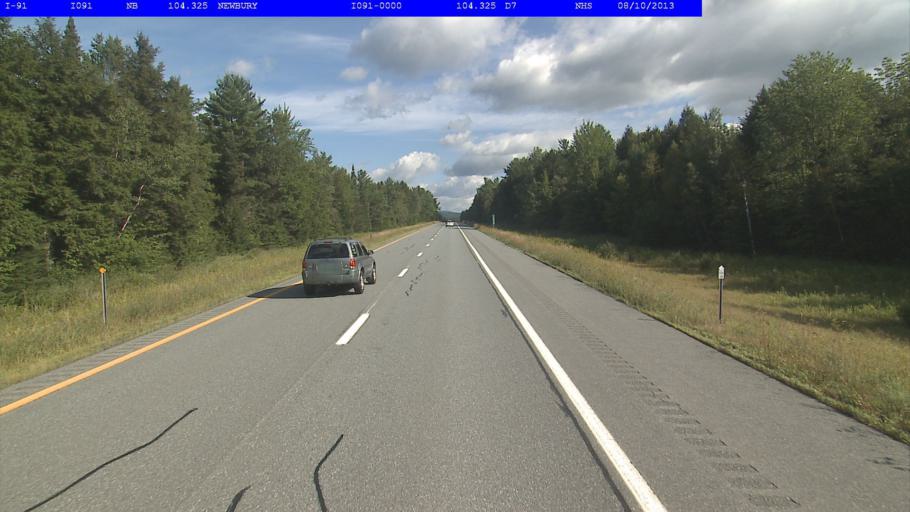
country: US
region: New Hampshire
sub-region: Grafton County
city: Haverhill
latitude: 44.0757
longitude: -72.1111
